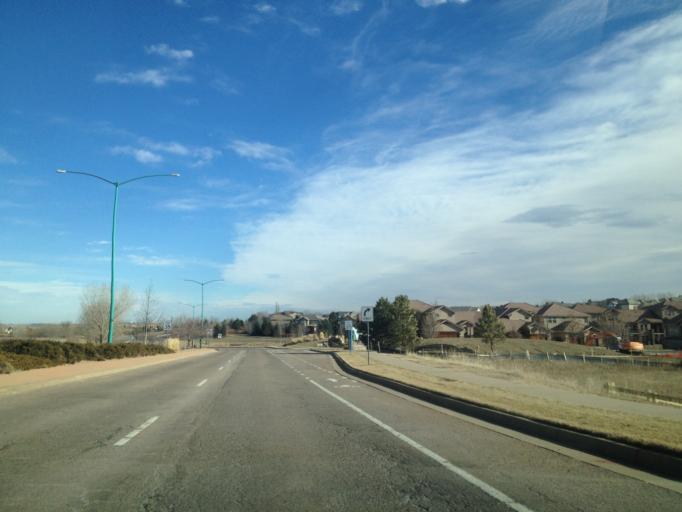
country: US
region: Colorado
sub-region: Boulder County
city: Superior
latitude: 39.9287
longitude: -105.1638
